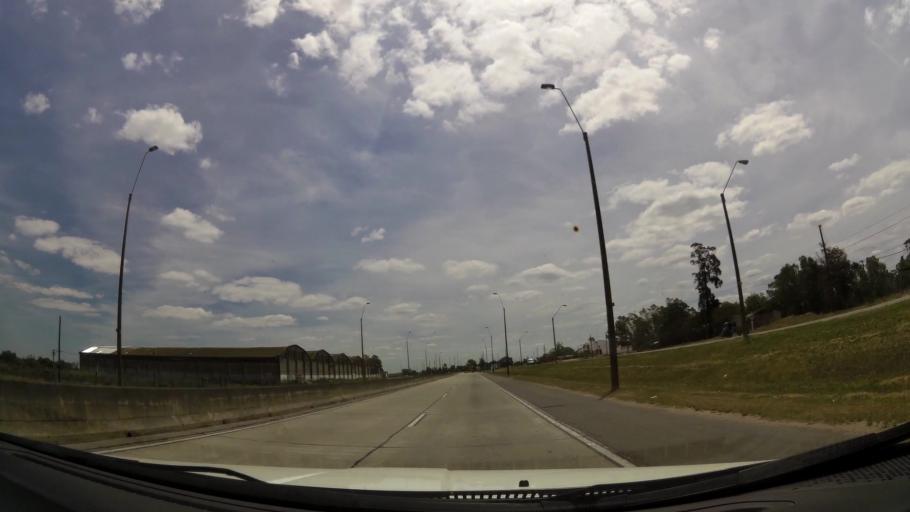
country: UY
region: San Jose
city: Delta del Tigre
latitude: -34.7699
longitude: -56.3881
